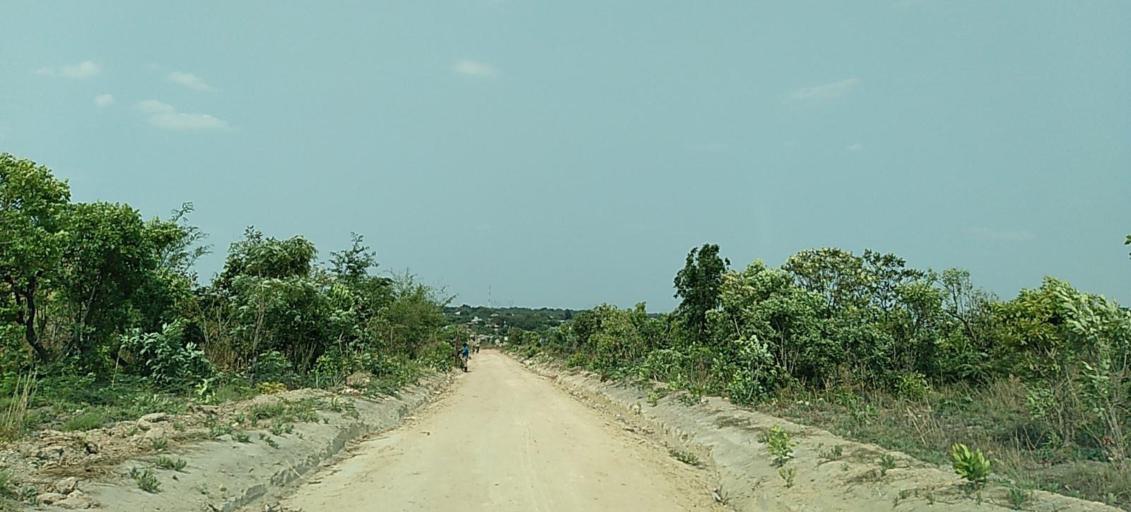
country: ZM
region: Copperbelt
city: Chambishi
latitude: -12.6236
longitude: 28.0831
